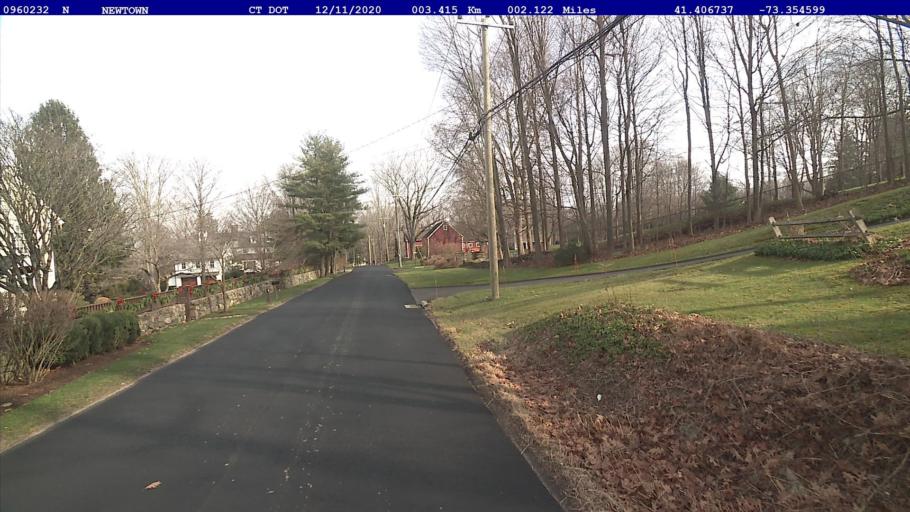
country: US
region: Connecticut
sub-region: Fairfield County
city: Newtown
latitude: 41.4067
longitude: -73.3546
